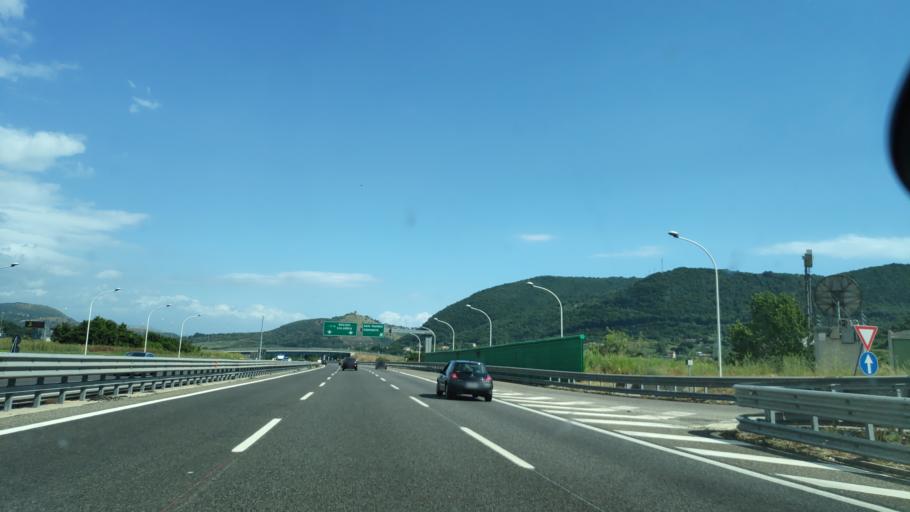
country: IT
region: Campania
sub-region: Provincia di Salerno
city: San Mango Piemonte
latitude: 40.6923
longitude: 14.8353
